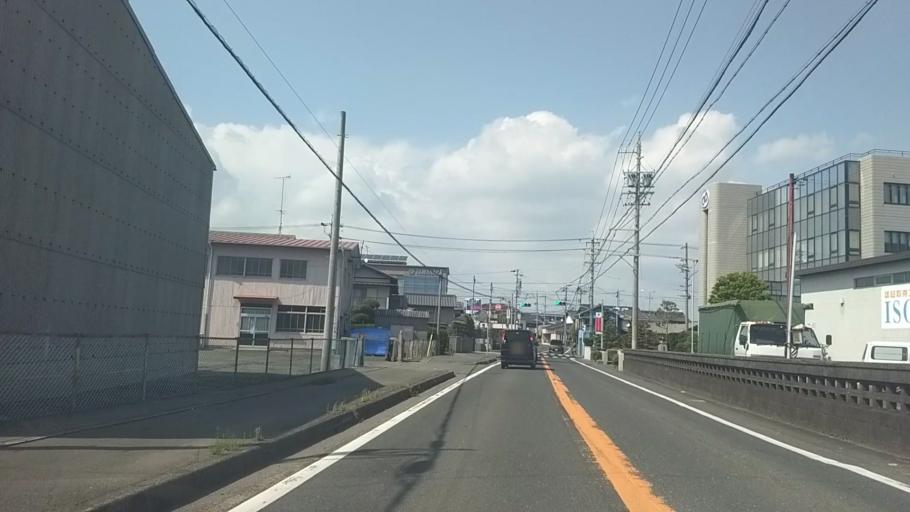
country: JP
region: Shizuoka
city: Hamamatsu
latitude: 34.6861
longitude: 137.7117
